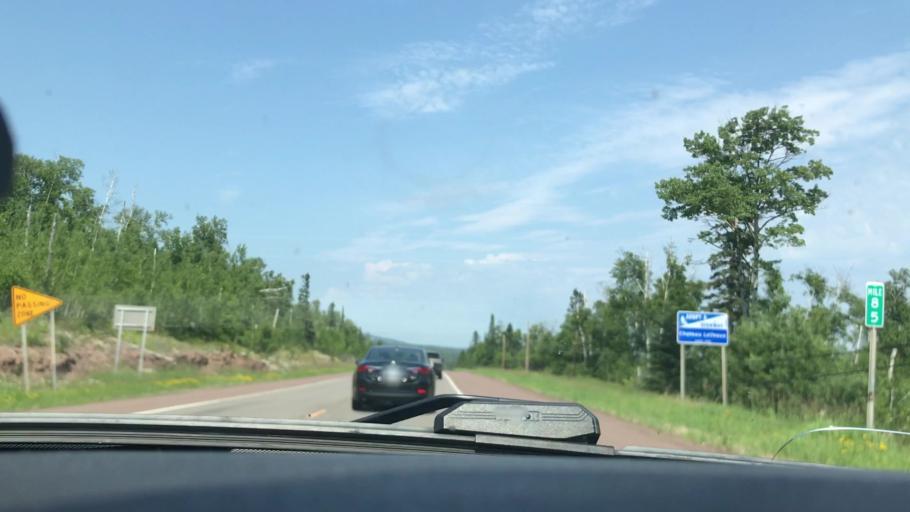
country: US
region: Minnesota
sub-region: Cook County
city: Grand Marais
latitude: 47.5956
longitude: -90.7947
